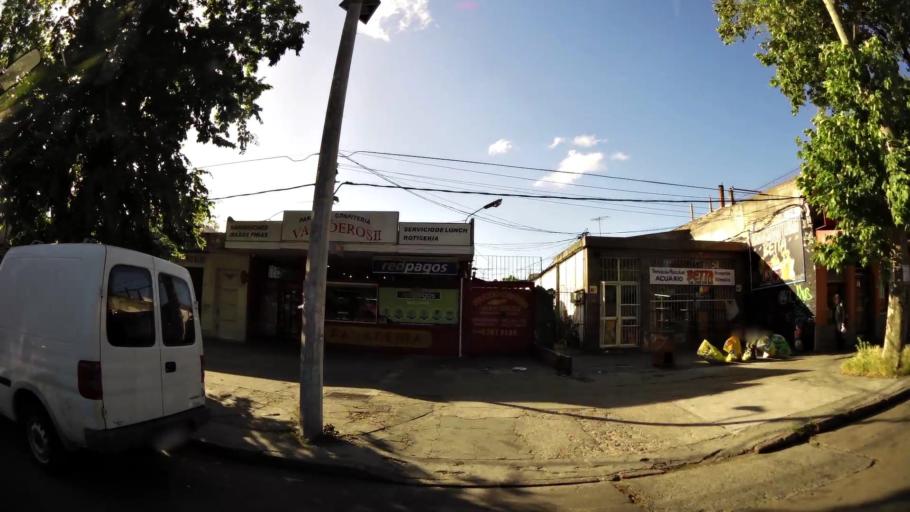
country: UY
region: Montevideo
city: Montevideo
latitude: -34.8607
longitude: -56.2295
